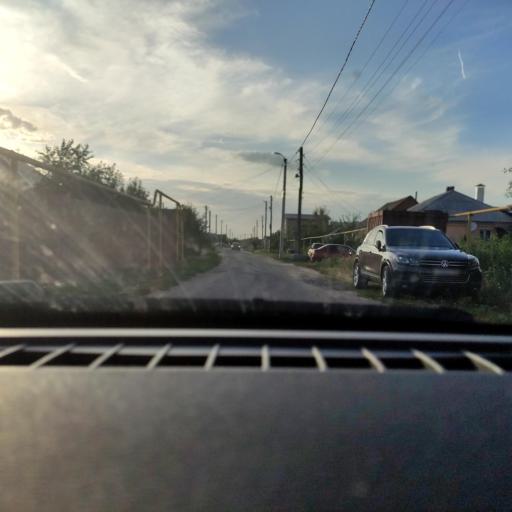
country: RU
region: Voronezj
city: Novaya Usman'
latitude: 51.6708
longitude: 39.3514
